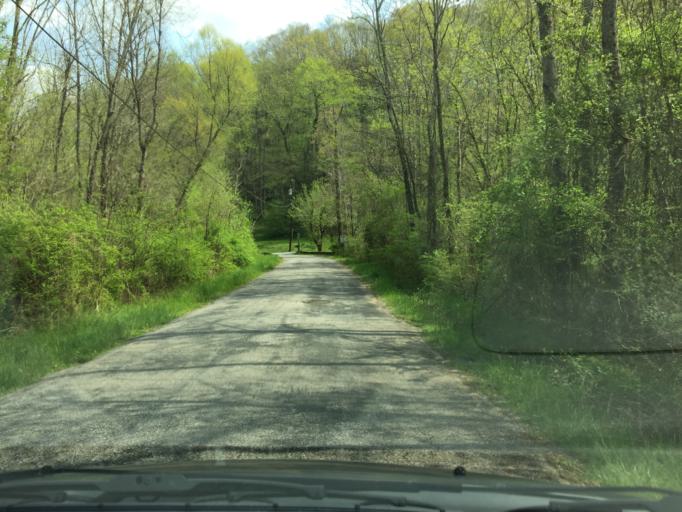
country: US
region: Tennessee
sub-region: Hamilton County
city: Falling Water
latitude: 35.1836
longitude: -85.2510
